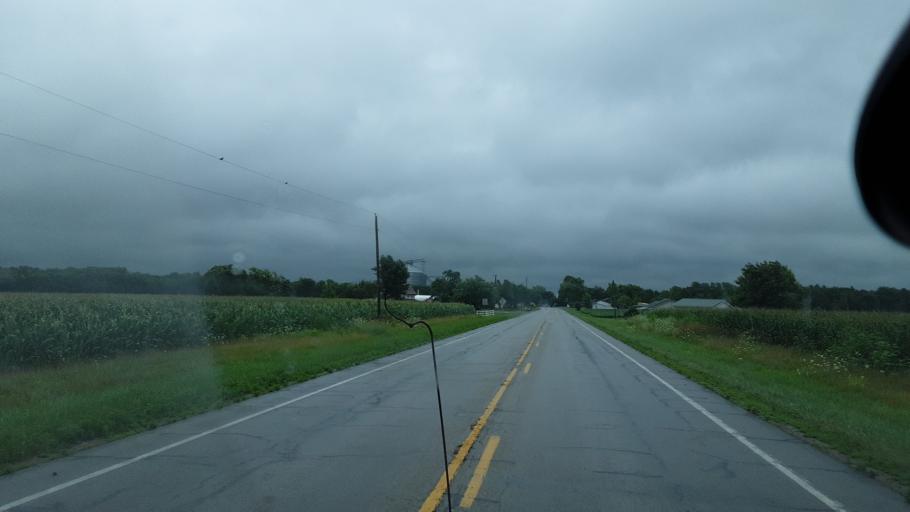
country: US
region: Indiana
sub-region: Adams County
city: Decatur
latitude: 40.7554
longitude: -84.8056
